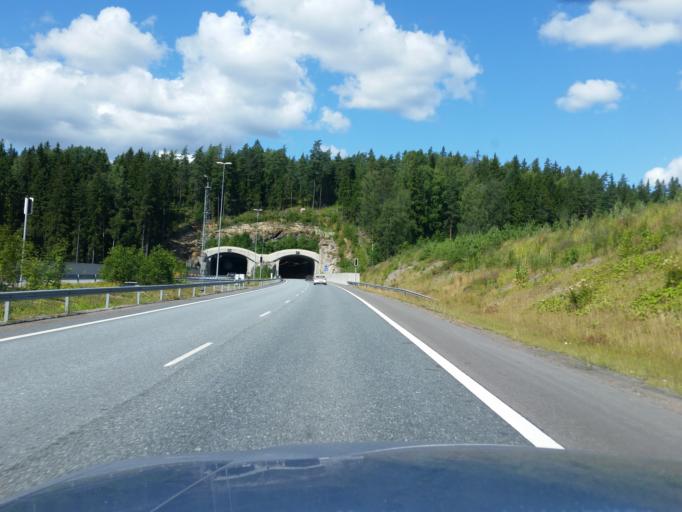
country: FI
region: Uusimaa
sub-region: Helsinki
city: Lohja
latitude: 60.3039
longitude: 24.0472
